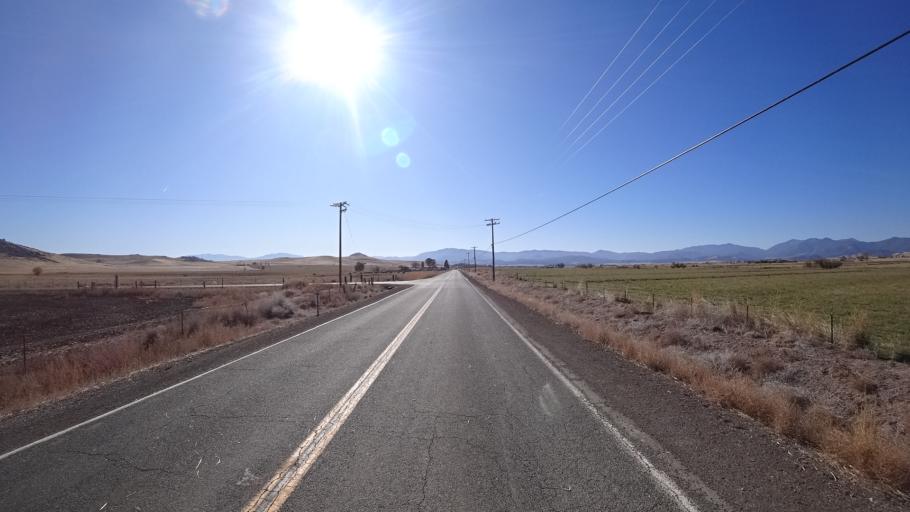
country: US
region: California
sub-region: Siskiyou County
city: Montague
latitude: 41.7566
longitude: -122.4945
